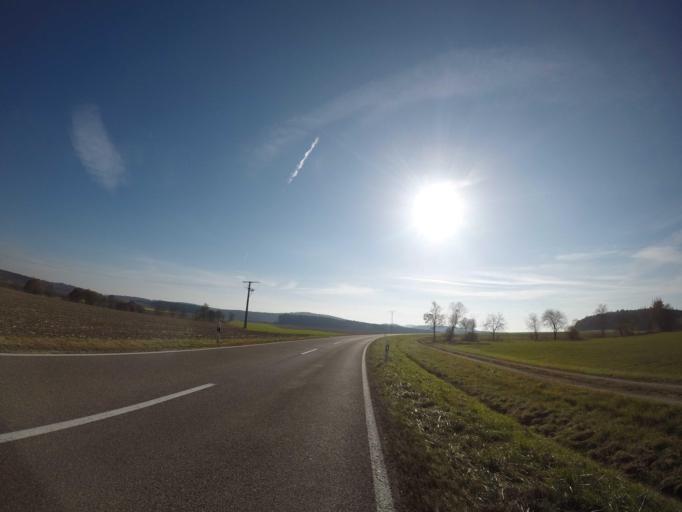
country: DE
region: Baden-Wuerttemberg
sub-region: Tuebingen Region
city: Obermarchtal
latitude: 48.2232
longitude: 9.5651
